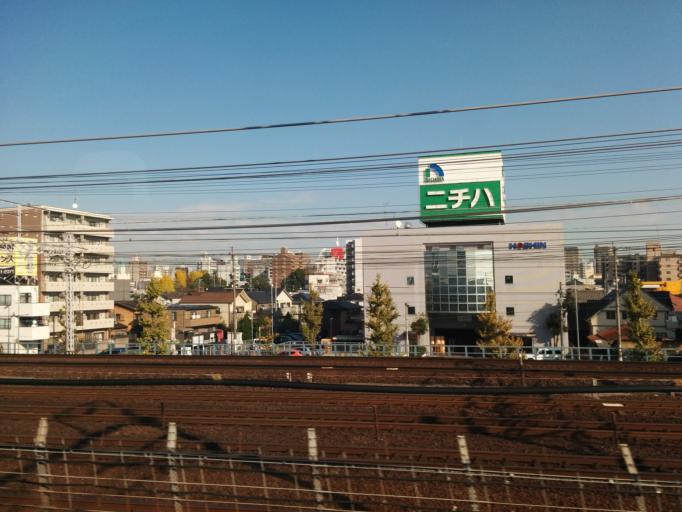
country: JP
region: Aichi
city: Nagoya-shi
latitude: 35.1562
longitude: 136.8872
